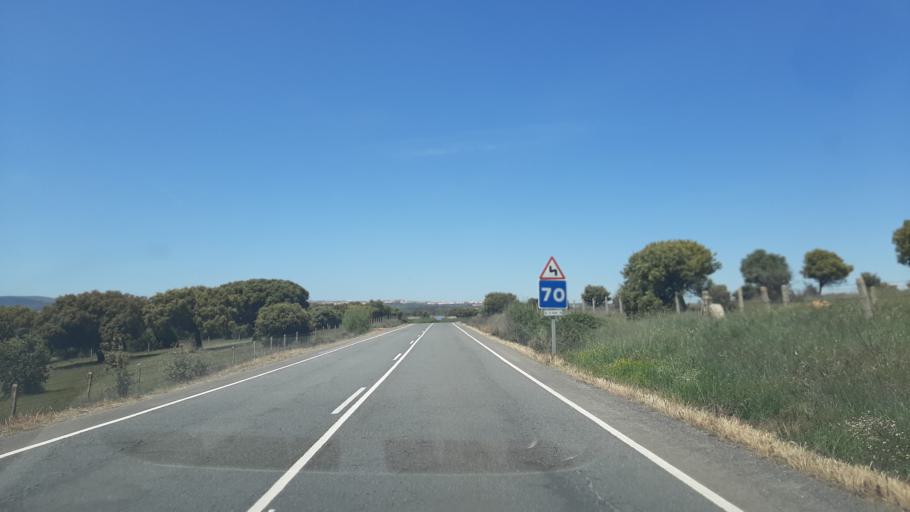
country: ES
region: Castille and Leon
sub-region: Provincia de Salamanca
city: Aldeavieja de Tormes
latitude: 40.5493
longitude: -5.6049
